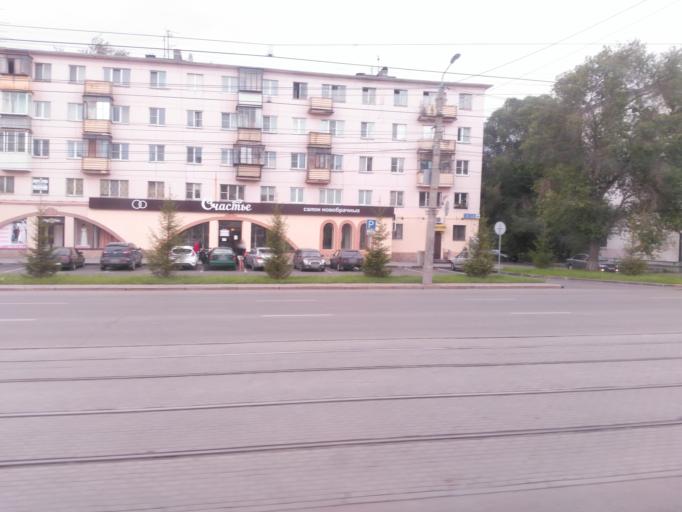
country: RU
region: Chelyabinsk
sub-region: Gorod Chelyabinsk
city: Chelyabinsk
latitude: 55.1826
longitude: 61.3988
